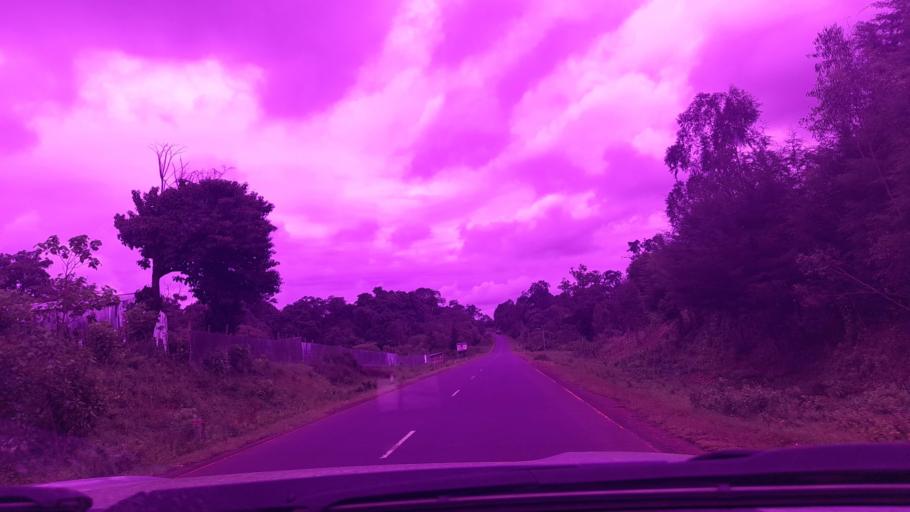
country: ET
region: Southern Nations, Nationalities, and People's Region
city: Bonga
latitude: 7.2798
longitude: 35.9491
